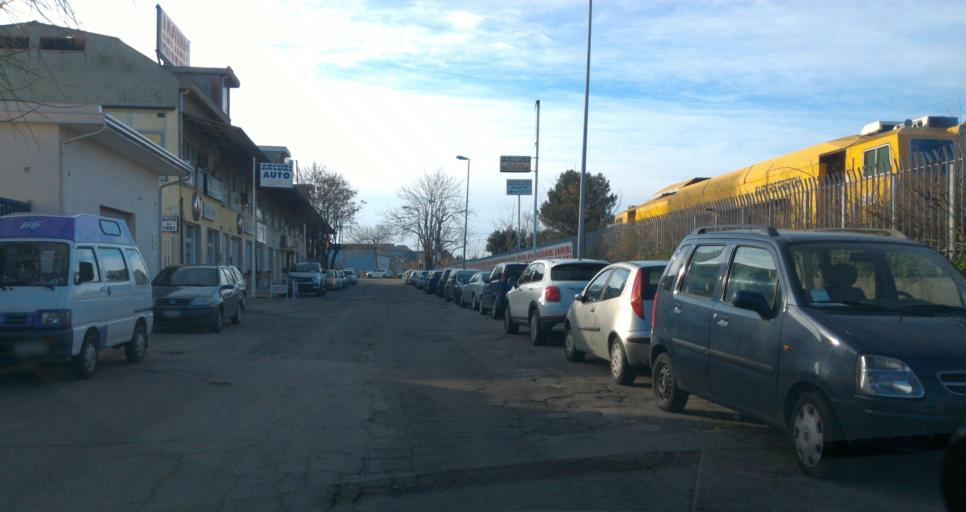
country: IT
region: Calabria
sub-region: Provincia di Crotone
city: Crotone
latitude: 39.0854
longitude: 17.1107
